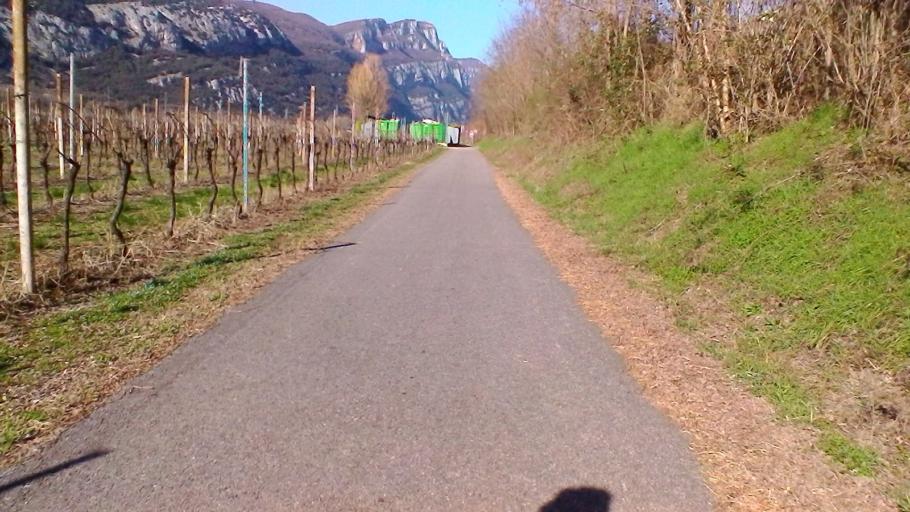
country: IT
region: Veneto
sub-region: Provincia di Verona
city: Dolce
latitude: 45.5894
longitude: 10.8462
